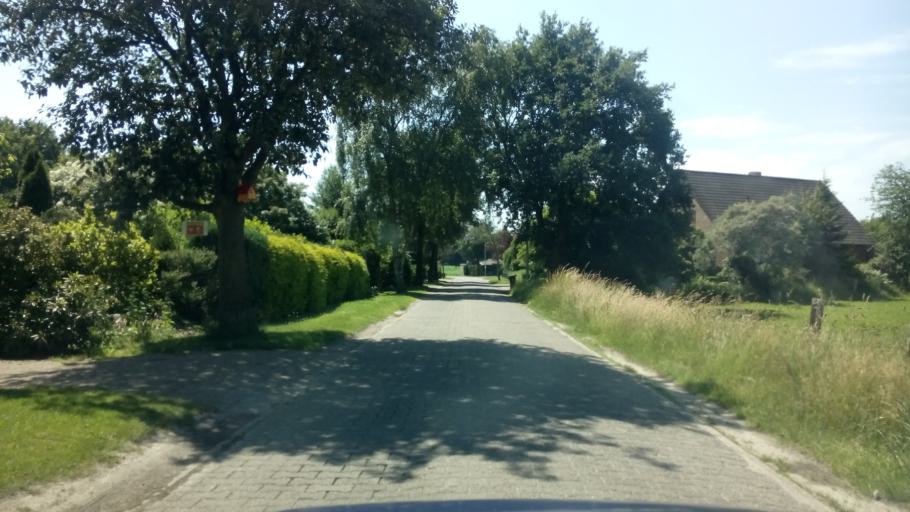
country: DE
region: Lower Saxony
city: Hambergen
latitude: 53.2676
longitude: 8.8208
